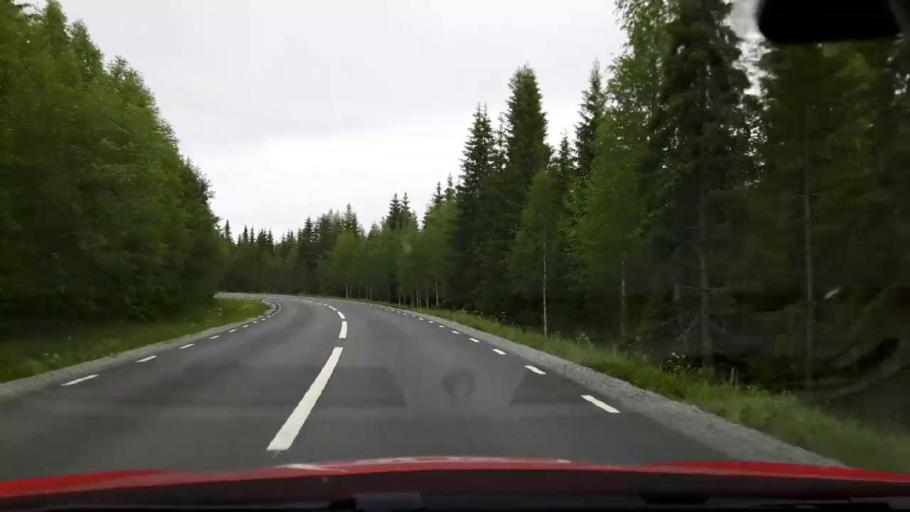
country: SE
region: Jaemtland
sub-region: OEstersunds Kommun
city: Lit
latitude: 63.7426
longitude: 14.8104
